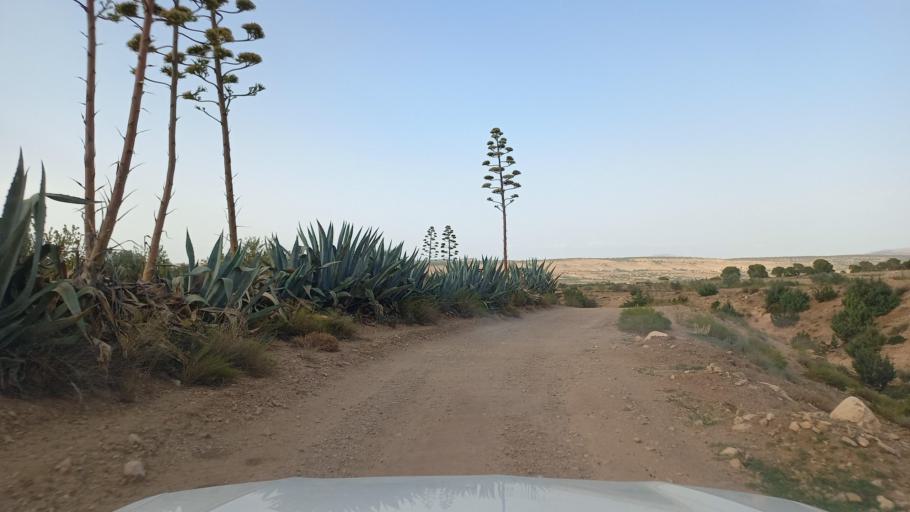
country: TN
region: Al Qasrayn
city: Kasserine
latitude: 35.3346
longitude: 8.8502
